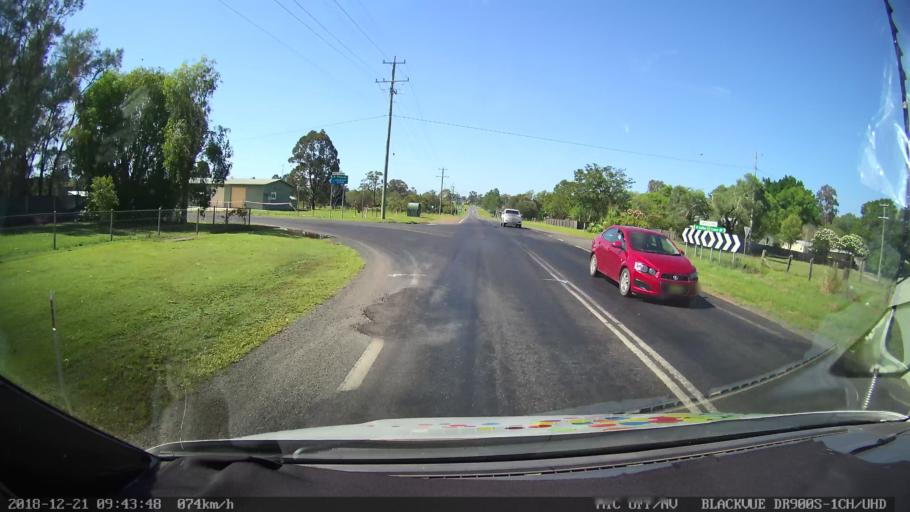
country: AU
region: New South Wales
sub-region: Clarence Valley
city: Grafton
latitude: -29.6108
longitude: 152.9352
